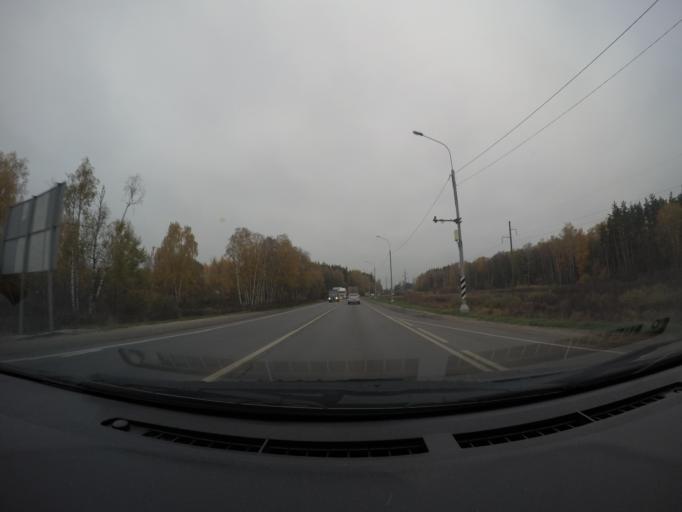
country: RU
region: Moskovskaya
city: Malyshevo
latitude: 55.4787
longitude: 38.3461
